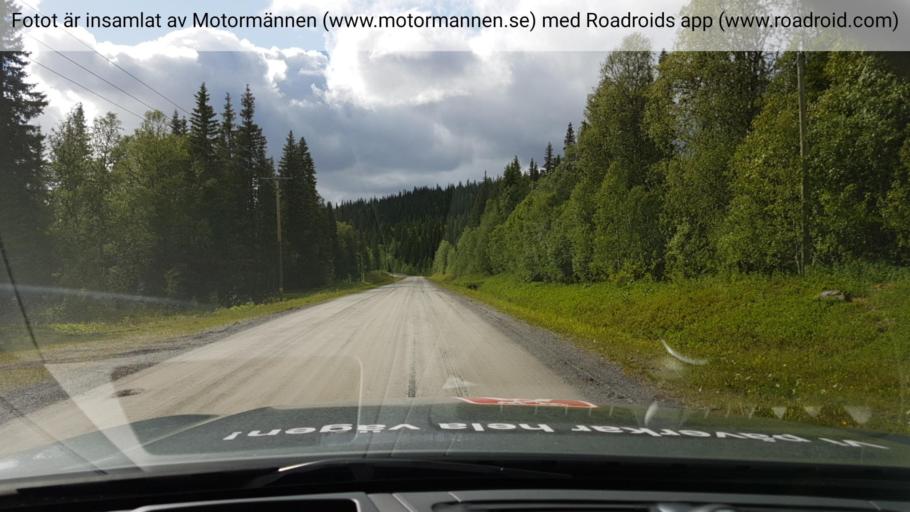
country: SE
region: Jaemtland
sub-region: Are Kommun
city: Are
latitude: 63.7051
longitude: 12.7512
